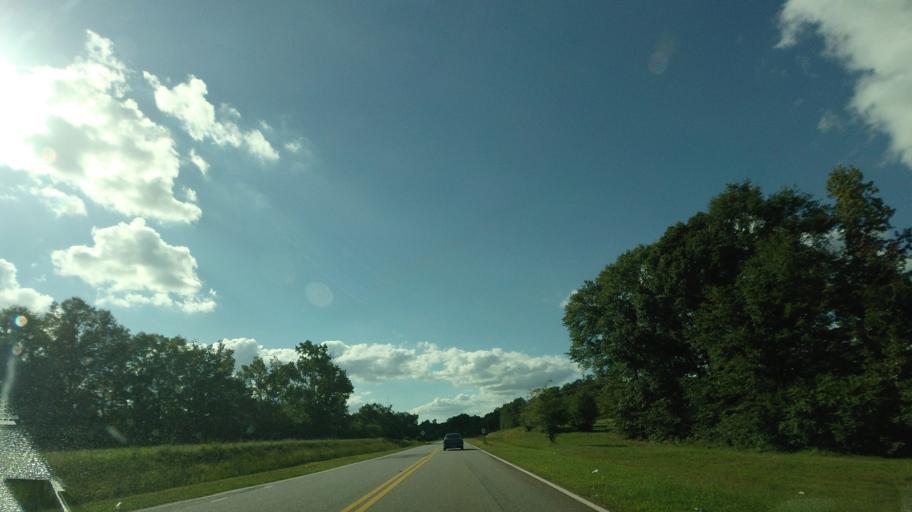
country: US
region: Georgia
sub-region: Lamar County
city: Barnesville
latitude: 33.0420
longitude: -84.1346
